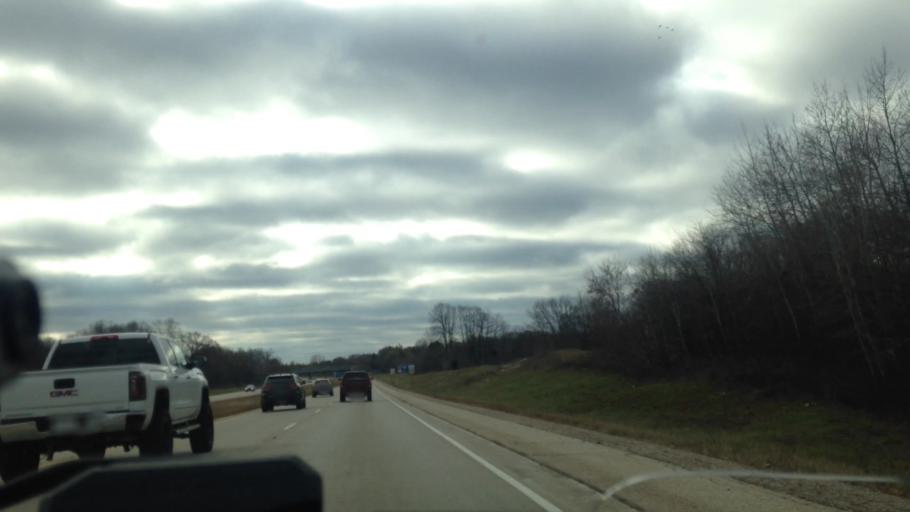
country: US
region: Wisconsin
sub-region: Washington County
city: West Bend
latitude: 43.4195
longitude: -88.2074
